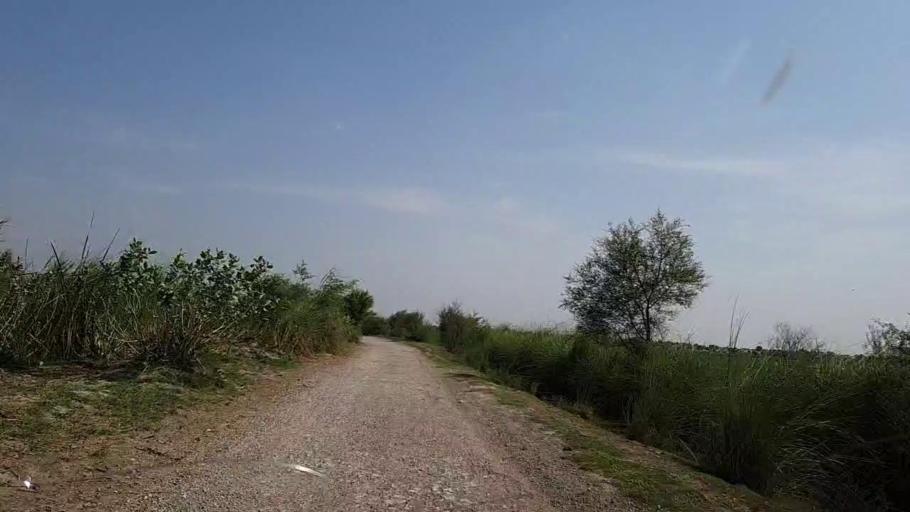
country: PK
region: Sindh
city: Khanpur
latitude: 27.7195
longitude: 69.3609
